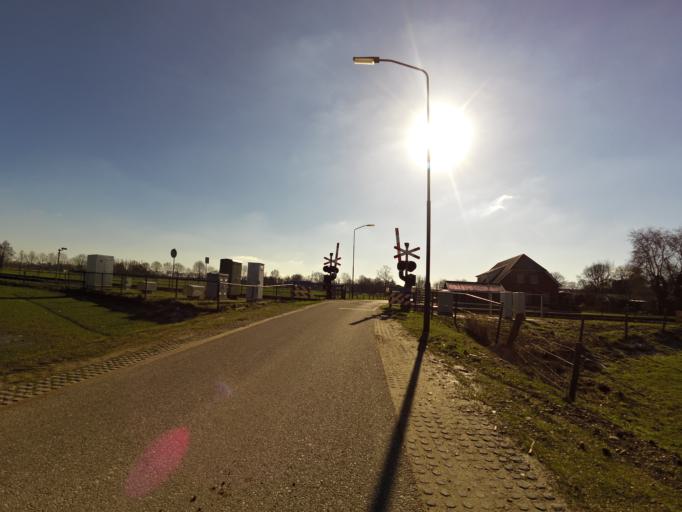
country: NL
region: Gelderland
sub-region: Gemeente Doetinchem
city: Doetinchem
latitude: 51.9584
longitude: 6.2257
